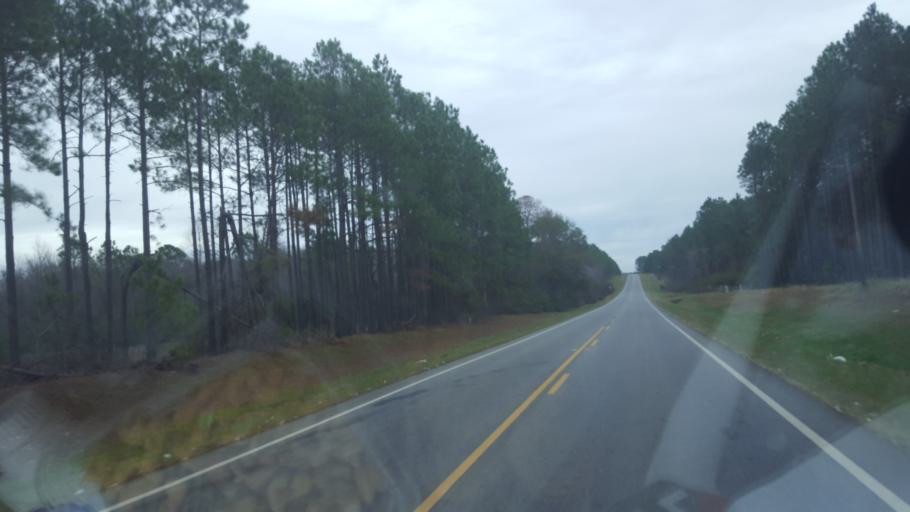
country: US
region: Georgia
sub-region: Turner County
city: Ashburn
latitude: 31.7158
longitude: -83.6210
